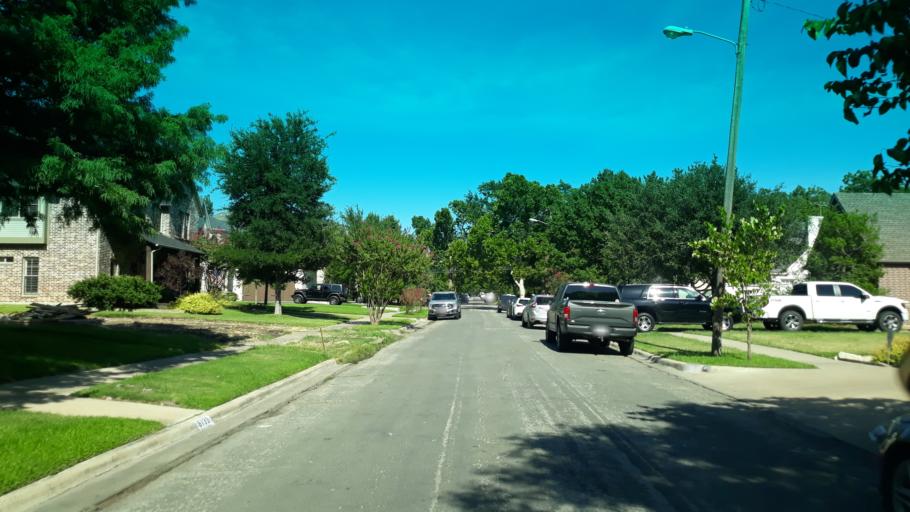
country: US
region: Texas
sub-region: Dallas County
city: Highland Park
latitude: 32.8201
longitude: -96.7601
